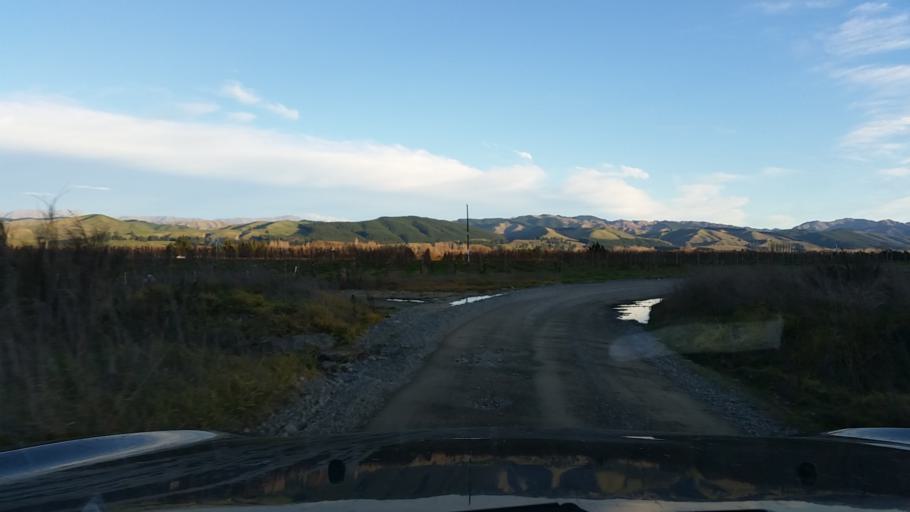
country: NZ
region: Marlborough
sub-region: Marlborough District
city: Blenheim
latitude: -41.5168
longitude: 173.5849
